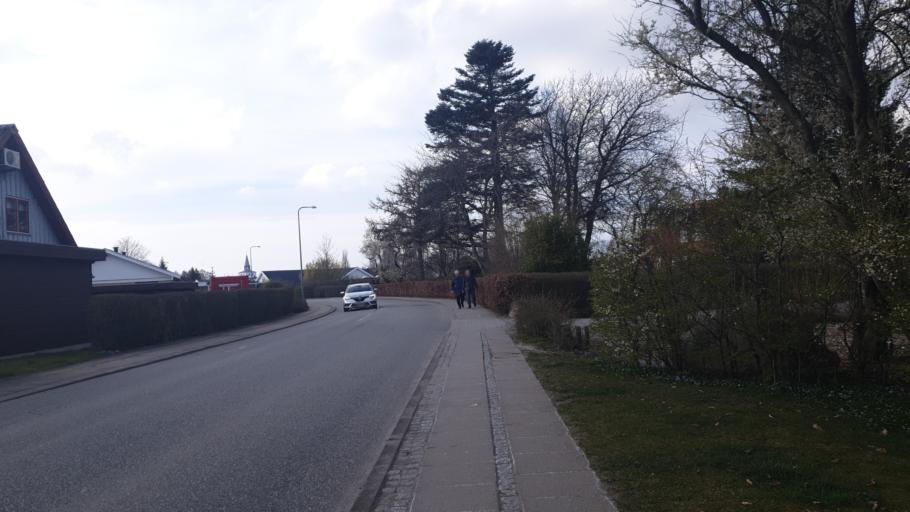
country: DK
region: Central Jutland
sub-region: Hedensted Kommune
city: Hedensted
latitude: 55.7668
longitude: 9.7103
